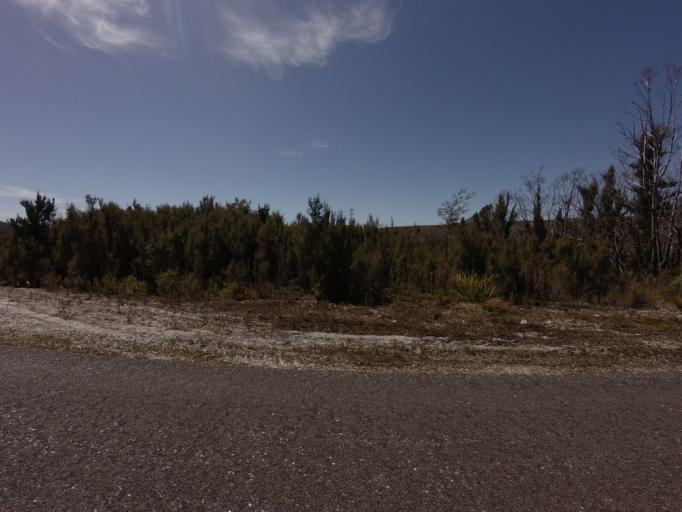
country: AU
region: Tasmania
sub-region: Huon Valley
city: Geeveston
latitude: -42.8548
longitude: 146.1886
